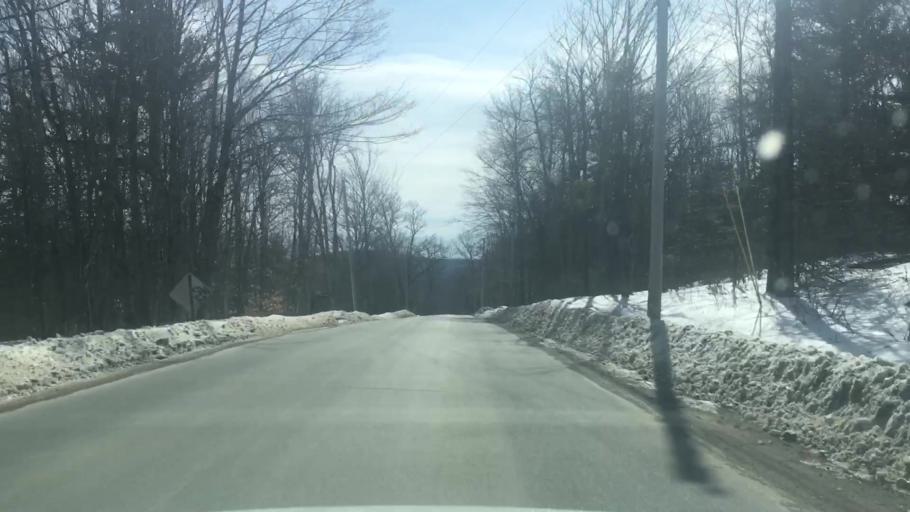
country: US
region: Maine
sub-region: Penobscot County
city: Holden
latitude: 44.7627
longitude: -68.6421
